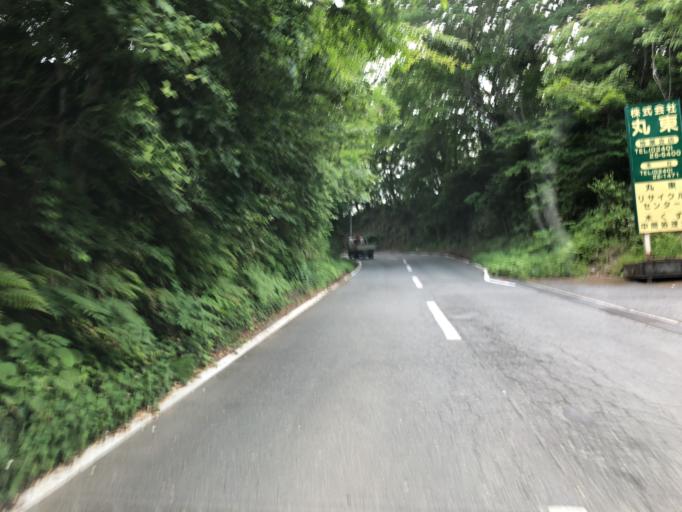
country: JP
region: Fukushima
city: Namie
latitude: 37.3102
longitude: 141.0054
